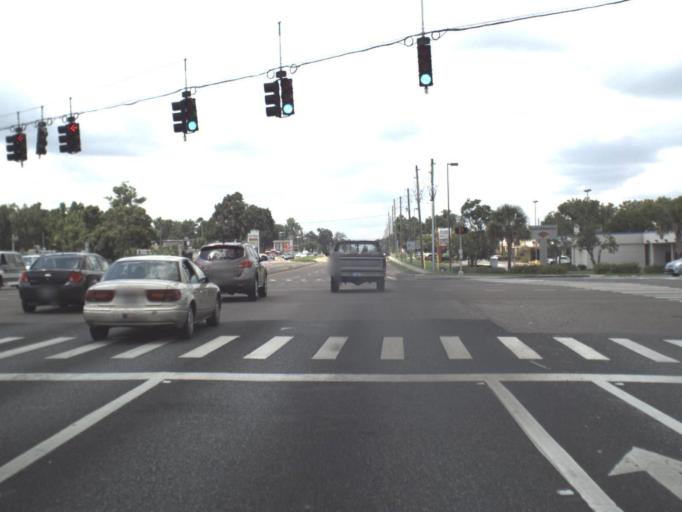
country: US
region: Florida
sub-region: Hernando County
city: South Brooksville
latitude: 28.5407
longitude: -82.4037
